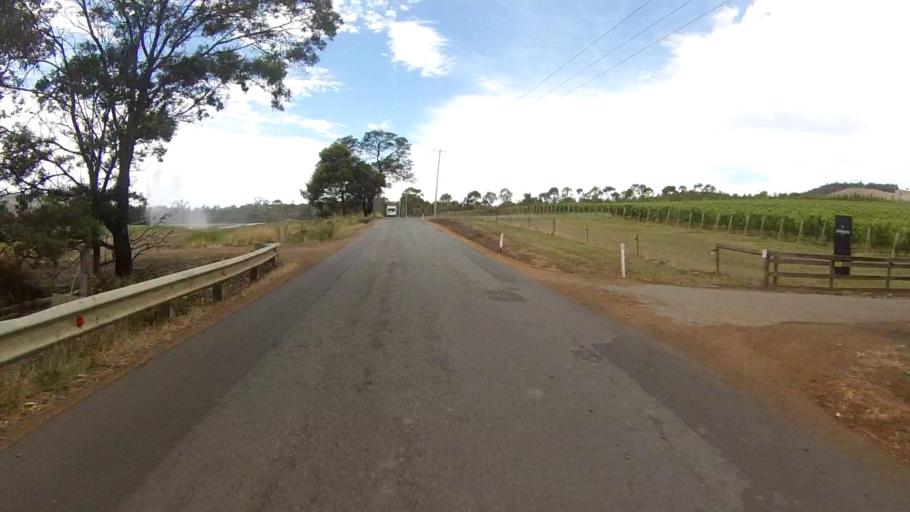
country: AU
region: Tasmania
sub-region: Clarence
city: Lindisfarne
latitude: -42.7615
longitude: 147.3891
